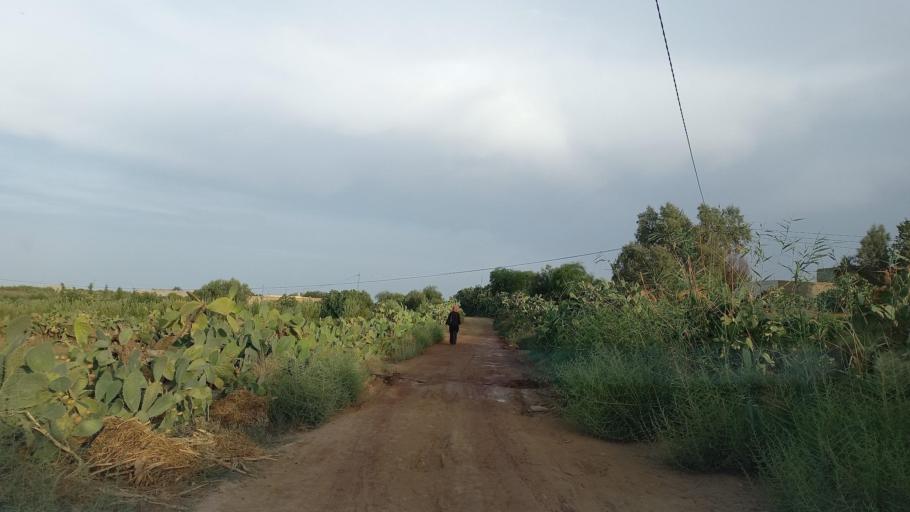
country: TN
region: Al Qasrayn
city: Kasserine
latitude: 35.2177
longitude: 9.0542
